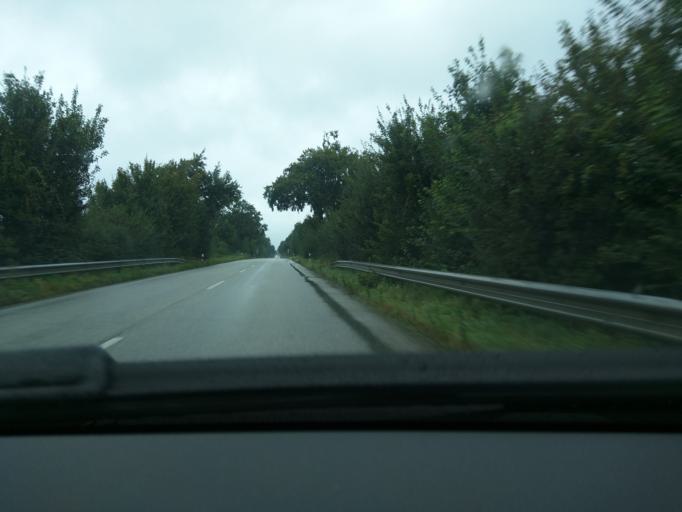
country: DE
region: Schleswig-Holstein
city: Kruzen
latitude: 53.3947
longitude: 10.5416
